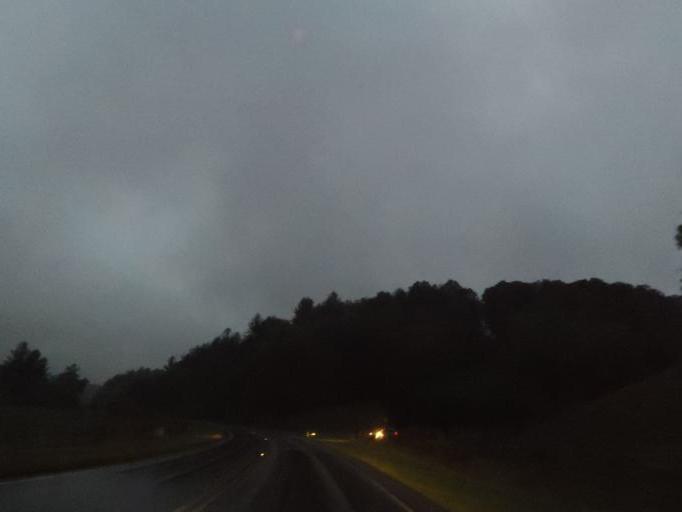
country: US
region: North Carolina
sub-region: Alleghany County
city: Sparta
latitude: 36.5488
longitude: -81.1521
